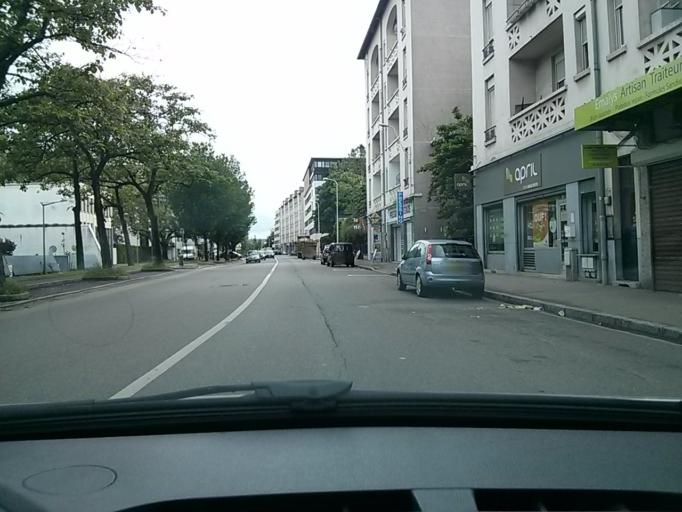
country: FR
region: Rhone-Alpes
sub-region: Departement du Rhone
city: Lyon
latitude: 45.7295
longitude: 4.8378
